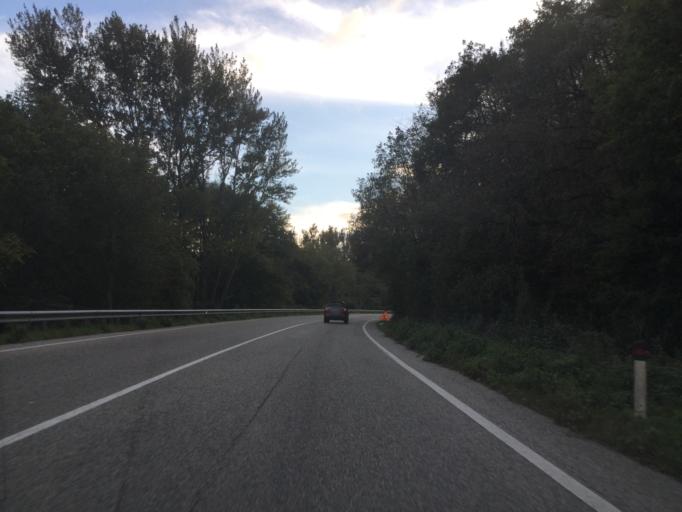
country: IT
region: The Marches
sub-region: Provincia di Ascoli Piceno
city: Arquata del Tronto
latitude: 42.7532
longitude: 13.2766
